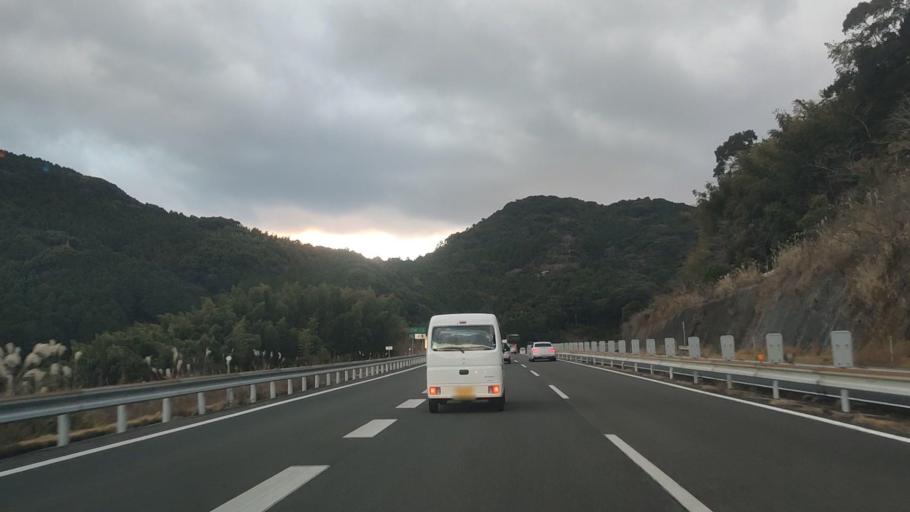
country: JP
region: Nagasaki
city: Obita
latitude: 32.8161
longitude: 129.9472
